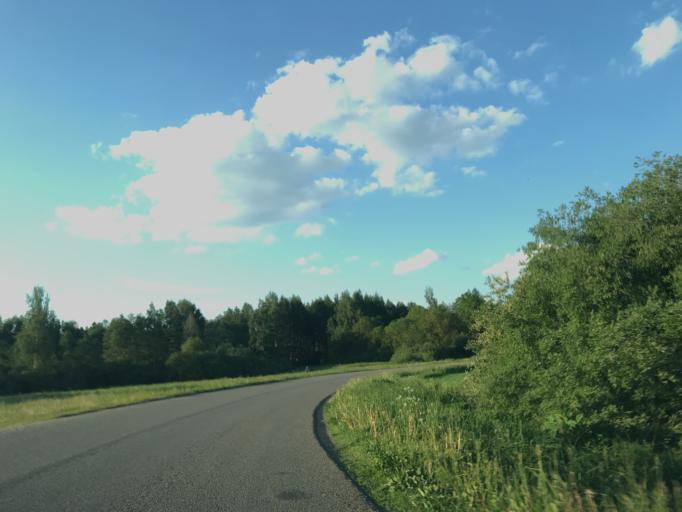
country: LV
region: Lecava
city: Iecava
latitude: 56.6161
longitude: 24.2455
